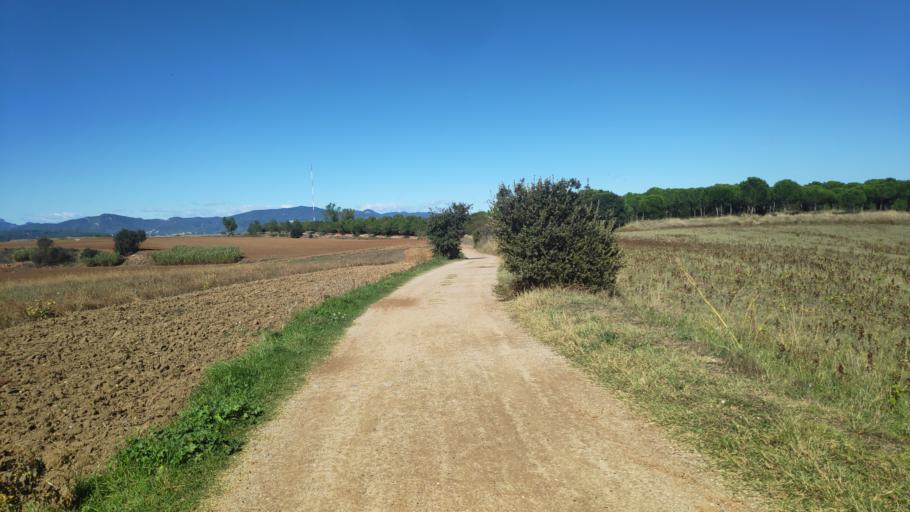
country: ES
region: Catalonia
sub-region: Provincia de Barcelona
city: Mollet del Valles
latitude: 41.5419
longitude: 2.1996
